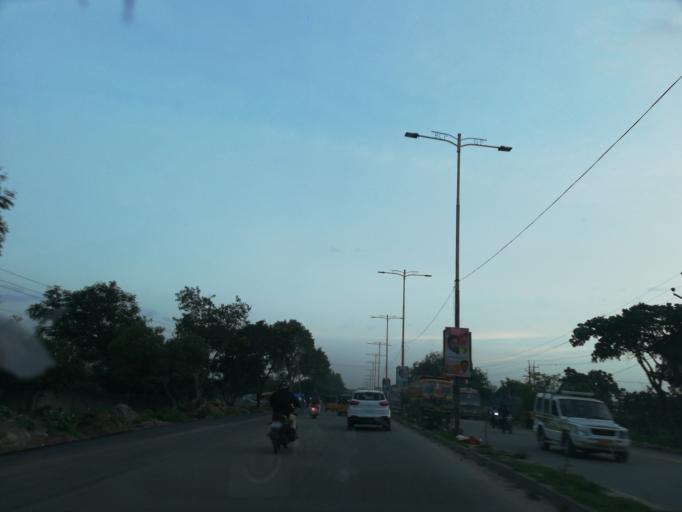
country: IN
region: Telangana
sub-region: Medak
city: Serilingampalle
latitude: 17.5387
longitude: 78.3589
